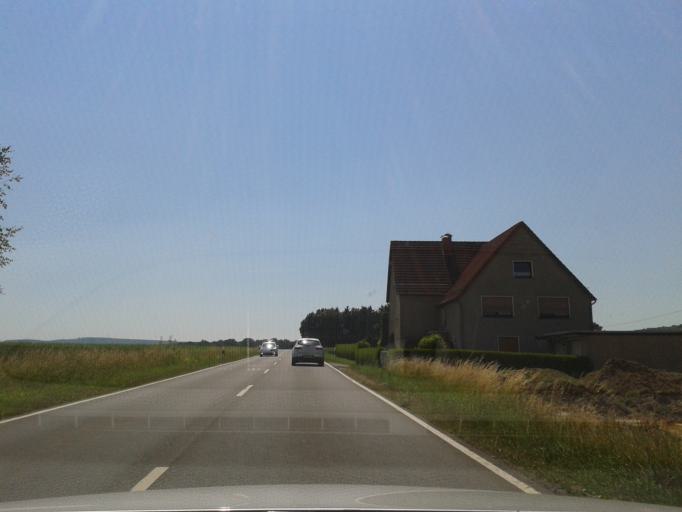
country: DE
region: North Rhine-Westphalia
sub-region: Regierungsbezirk Detmold
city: Barntrup
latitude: 52.0169
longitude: 9.0627
